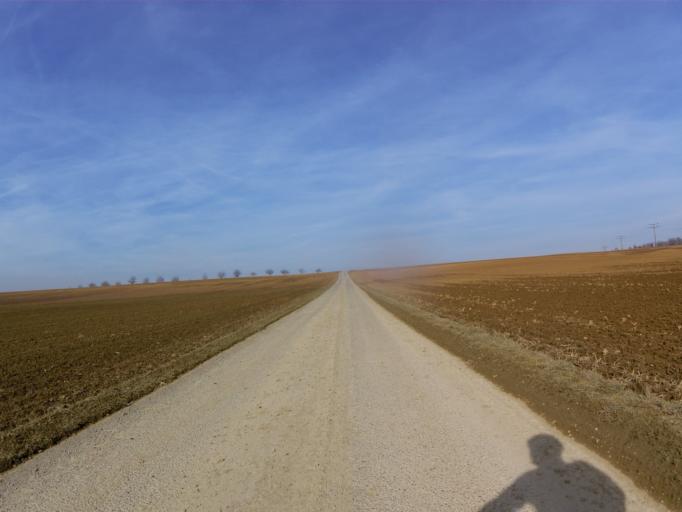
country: DE
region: Bavaria
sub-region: Regierungsbezirk Unterfranken
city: Kurnach
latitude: 49.8287
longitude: 10.0322
